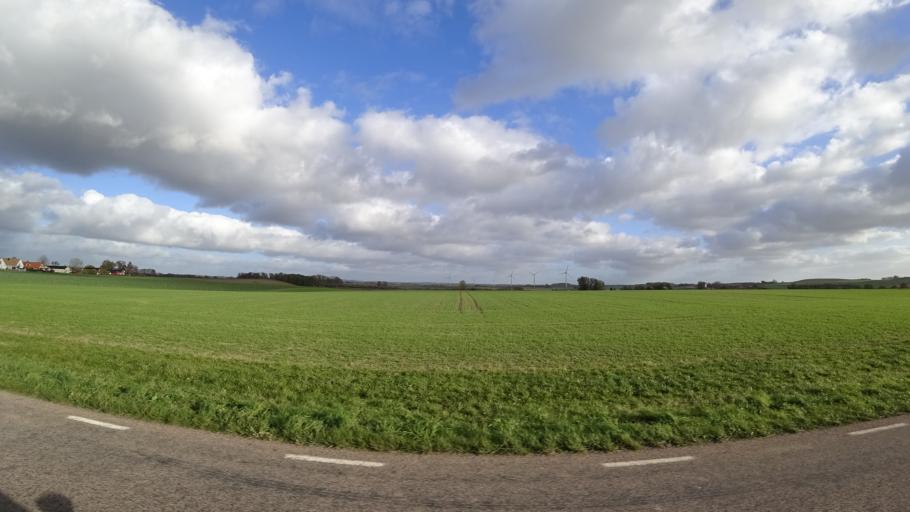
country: SE
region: Skane
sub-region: Staffanstorps Kommun
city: Staffanstorp
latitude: 55.6217
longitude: 13.2178
